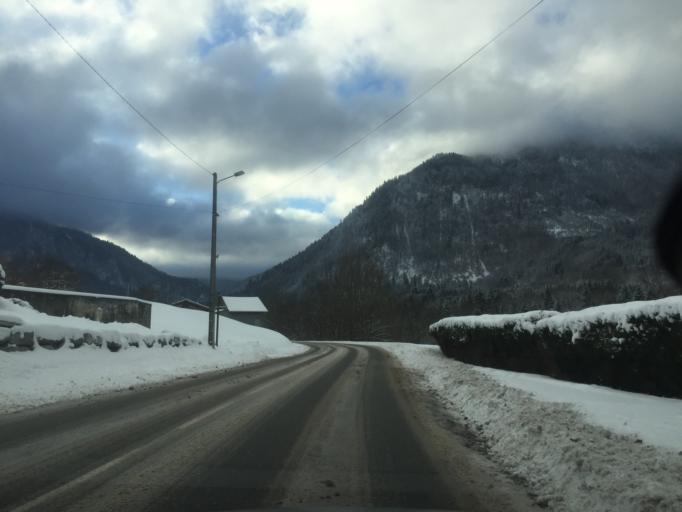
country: FR
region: Rhone-Alpes
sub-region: Departement de la Haute-Savoie
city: Saint-Paul-en-Chablais
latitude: 46.3259
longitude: 6.6695
